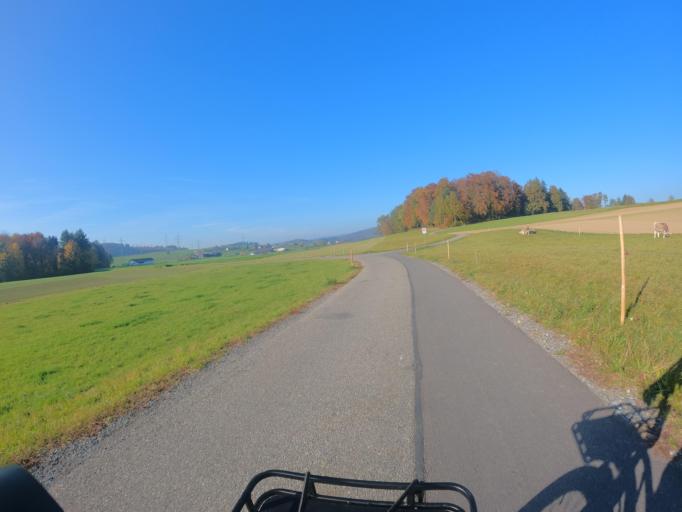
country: CH
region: Zurich
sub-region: Bezirk Affoltern
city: Affoltern / Oberdorf
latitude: 47.2797
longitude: 8.4360
